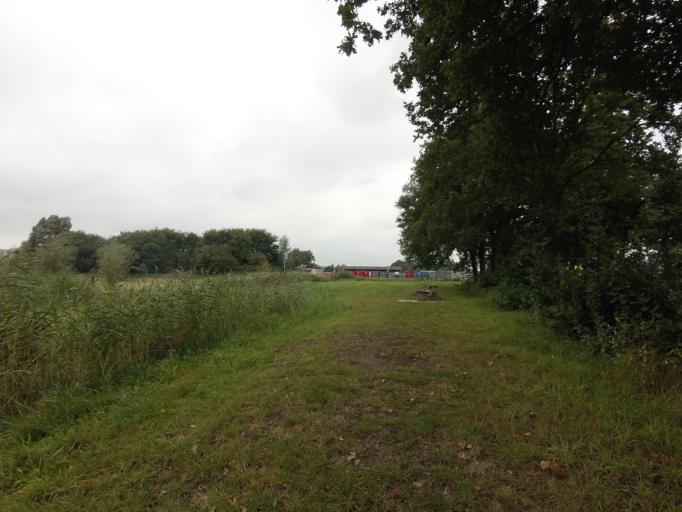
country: NL
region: Overijssel
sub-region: Gemeente Hengelo
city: Hengelo
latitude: 52.2758
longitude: 6.7731
